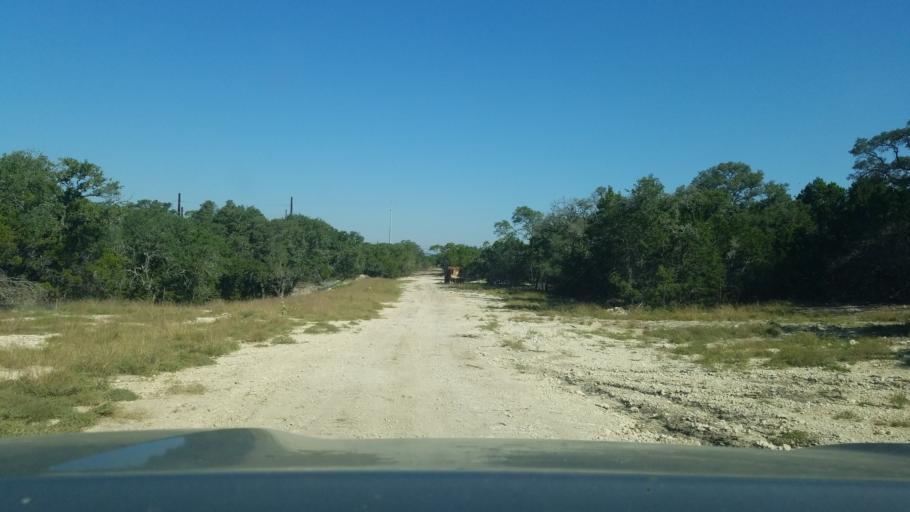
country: US
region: Texas
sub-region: Kendall County
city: Boerne
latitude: 29.7590
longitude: -98.7196
